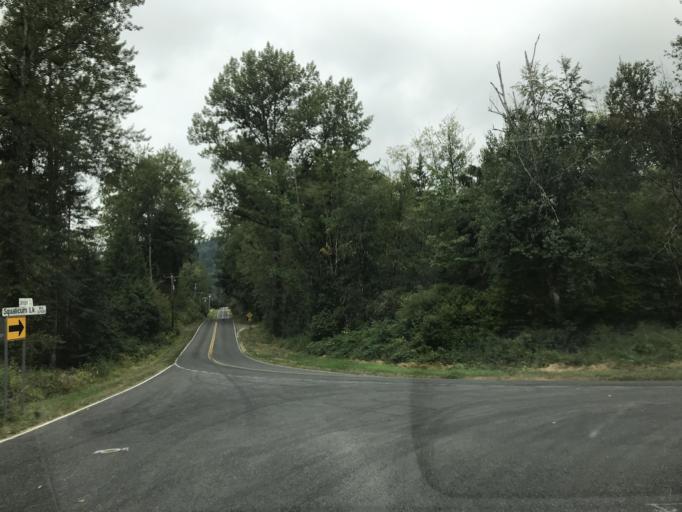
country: US
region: Washington
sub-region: Whatcom County
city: Sudden Valley
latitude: 48.7749
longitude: -122.3442
